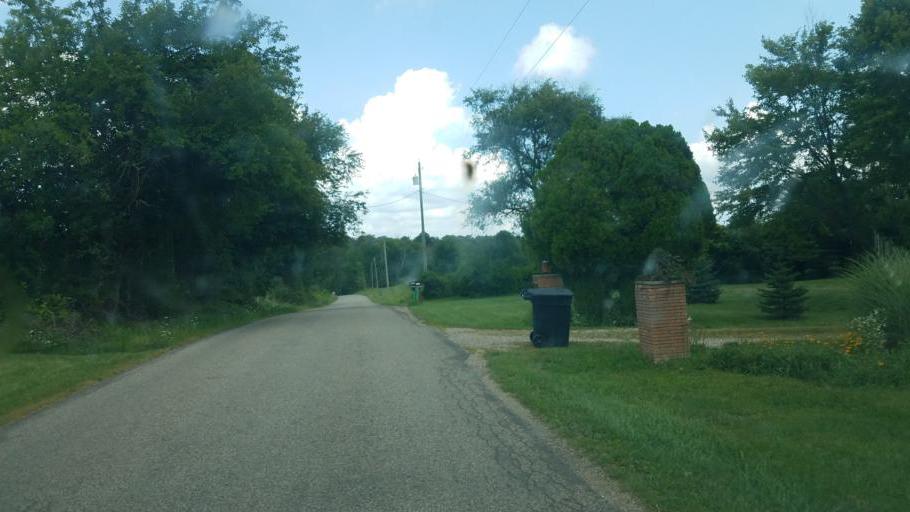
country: US
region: Ohio
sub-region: Knox County
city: Fredericktown
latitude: 40.3946
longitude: -82.6002
